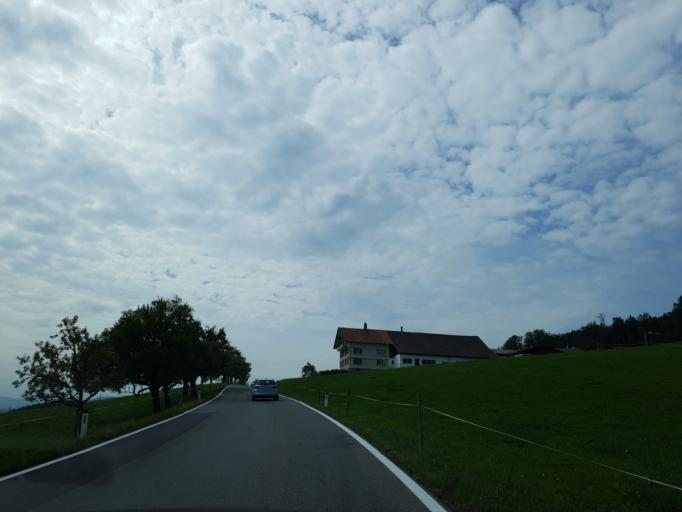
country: AT
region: Vorarlberg
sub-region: Politischer Bezirk Bregenz
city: Sulzberg
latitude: 47.4966
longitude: 9.9001
